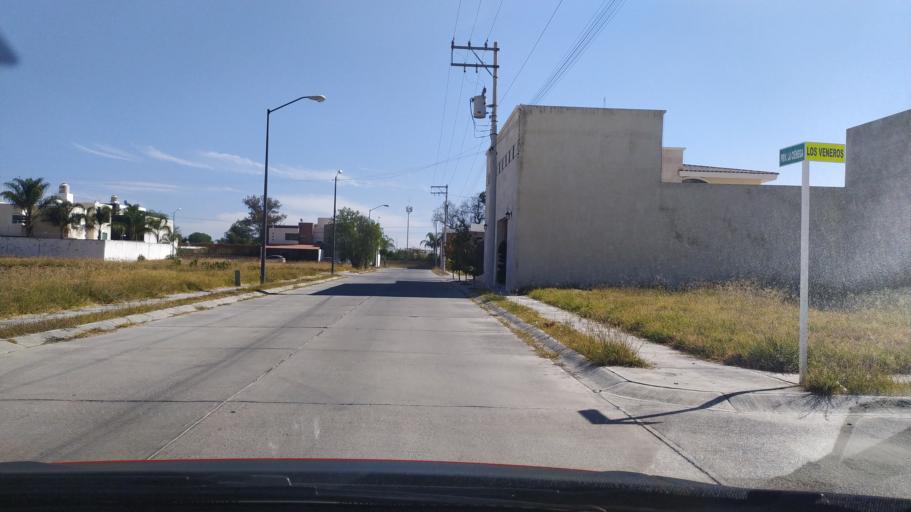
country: MX
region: Guanajuato
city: San Francisco del Rincon
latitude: 21.0242
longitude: -101.8734
